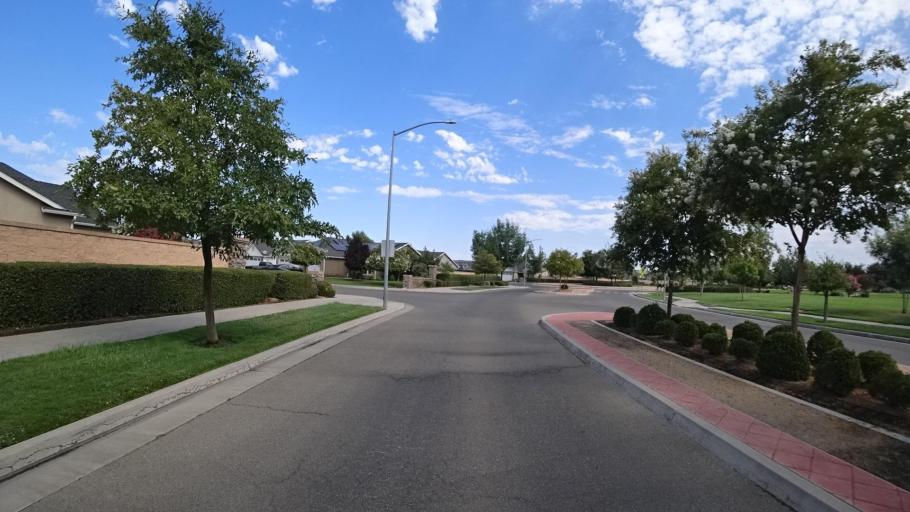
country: US
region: California
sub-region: Fresno County
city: Tarpey Village
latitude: 36.7818
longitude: -119.6691
